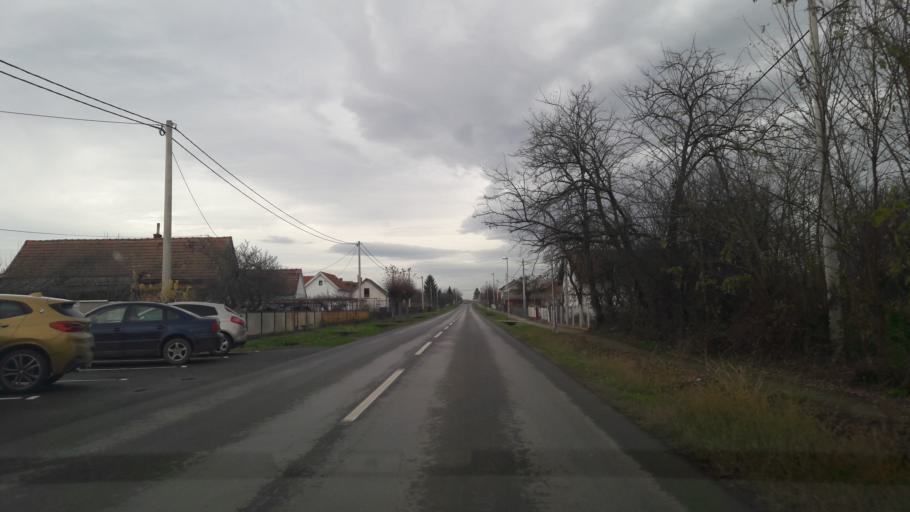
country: HR
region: Osjecko-Baranjska
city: Velimirovac
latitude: 45.5363
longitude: 18.0731
